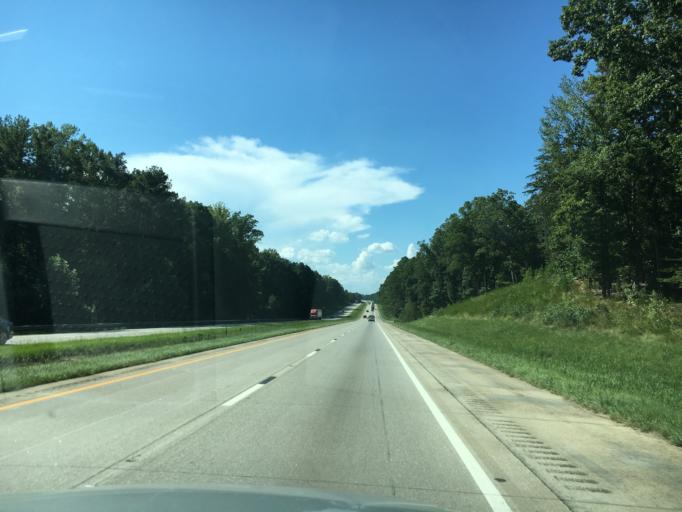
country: US
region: South Carolina
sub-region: Laurens County
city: Laurens
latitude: 34.5897
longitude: -82.0502
